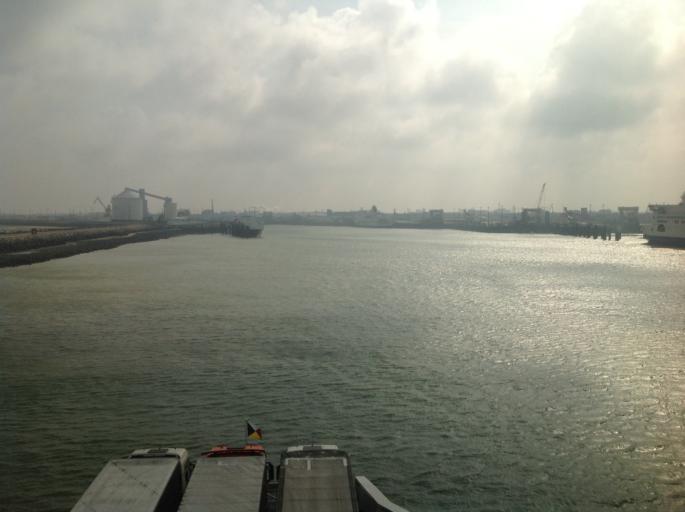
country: FR
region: Nord-Pas-de-Calais
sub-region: Departement du Pas-de-Calais
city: Calais
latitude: 50.9719
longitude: 1.8421
